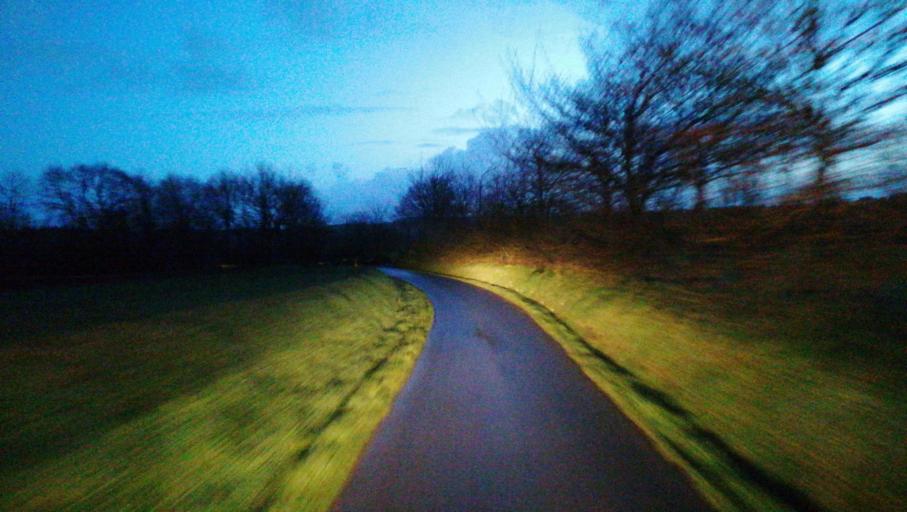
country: FR
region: Brittany
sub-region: Departement des Cotes-d'Armor
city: Plehedel
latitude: 48.6694
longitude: -3.0510
